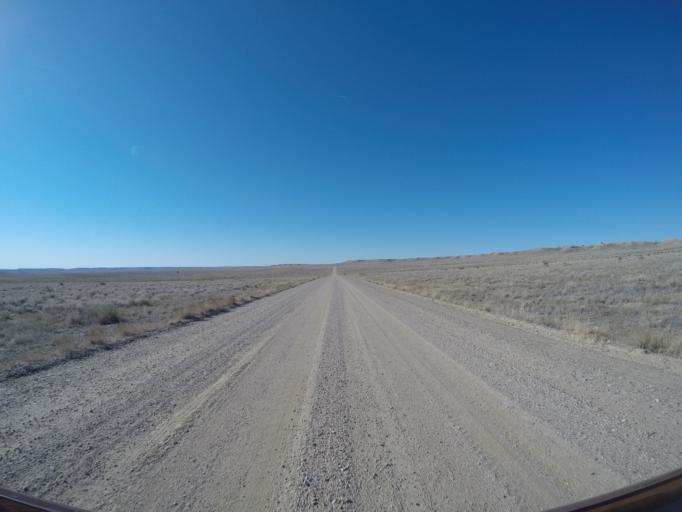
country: US
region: Colorado
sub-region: Otero County
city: La Junta
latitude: 37.7530
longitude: -103.6016
